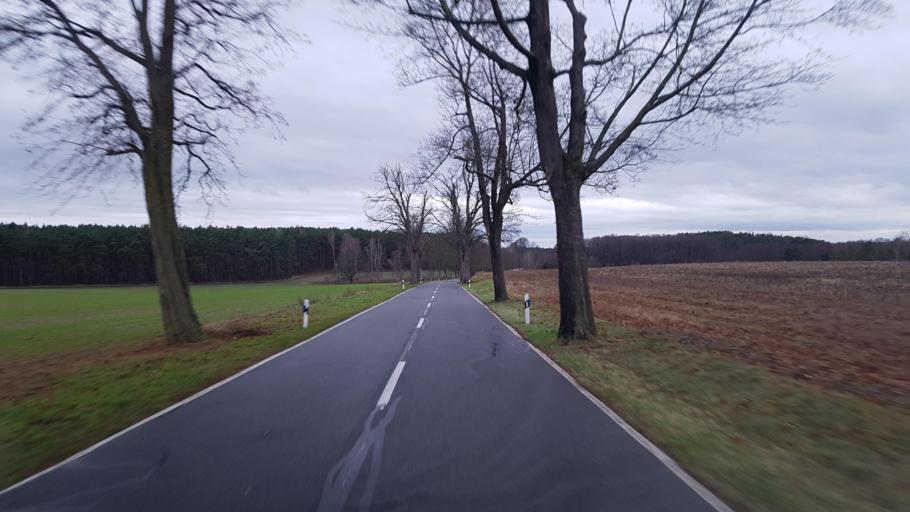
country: DE
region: Brandenburg
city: Wendisch Rietz
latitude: 52.0701
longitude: 14.0427
